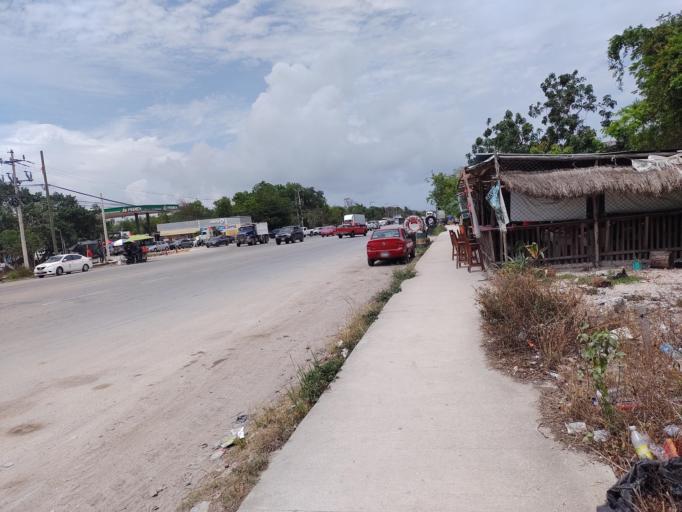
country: MX
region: Quintana Roo
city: Tulum
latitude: 20.2071
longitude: -87.4751
